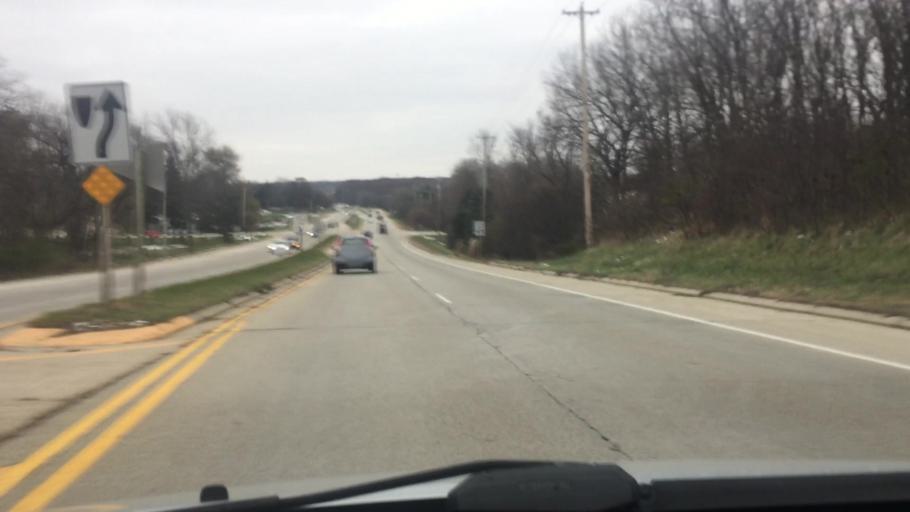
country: US
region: Wisconsin
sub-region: Waukesha County
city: Delafield
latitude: 43.0660
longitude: -88.3670
